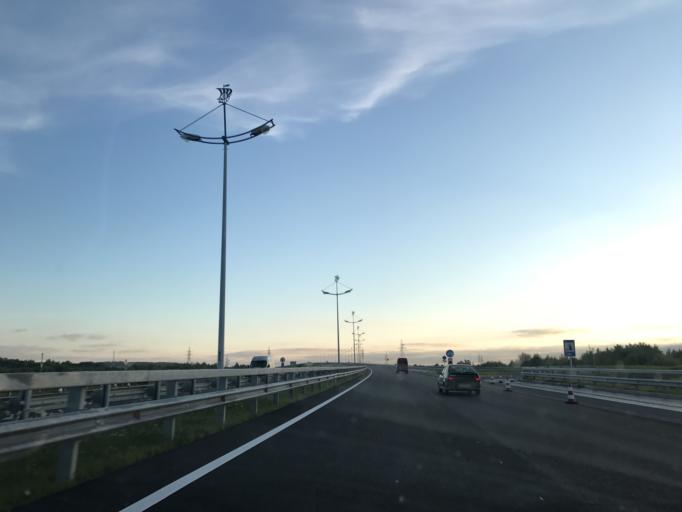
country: RU
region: Kaliningrad
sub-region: Gorod Kaliningrad
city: Pionerskiy
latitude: 54.9186
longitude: 20.2460
